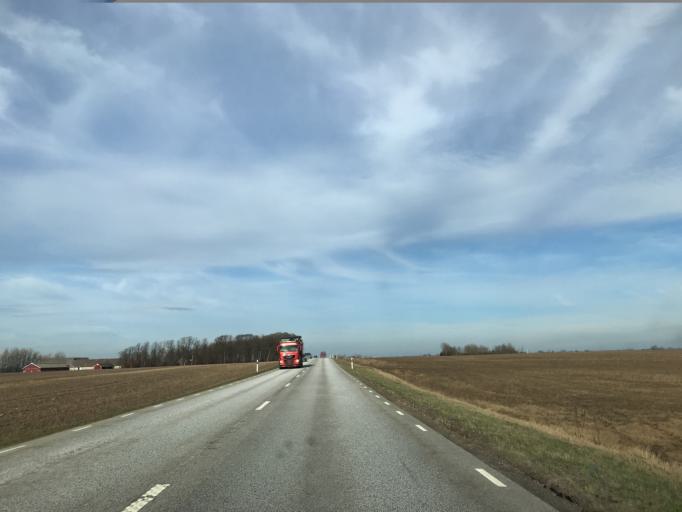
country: SE
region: Skane
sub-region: Tomelilla Kommun
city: Tomelilla
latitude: 55.5383
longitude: 13.9140
